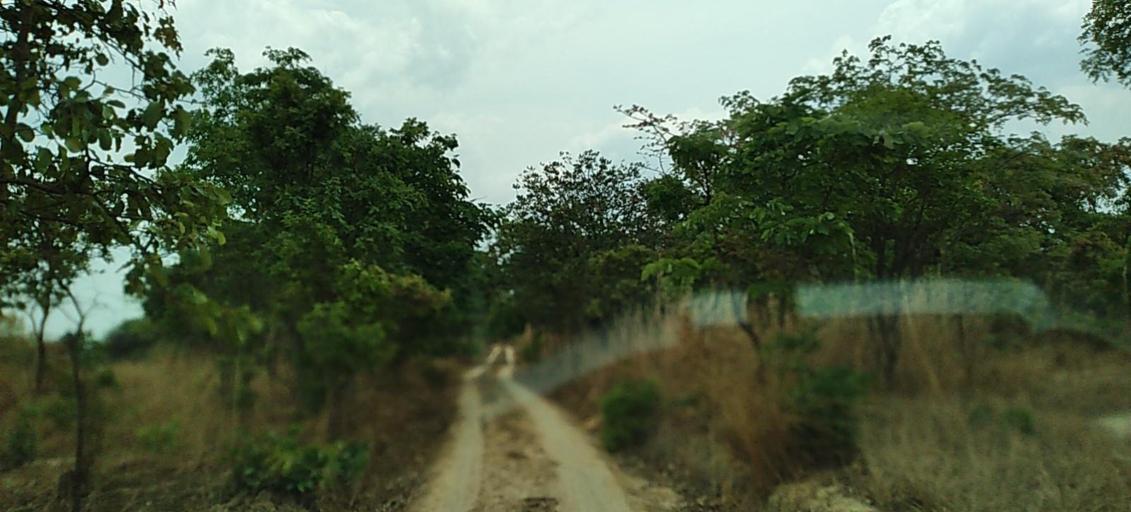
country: ZM
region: Copperbelt
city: Chililabombwe
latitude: -12.3235
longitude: 27.7825
